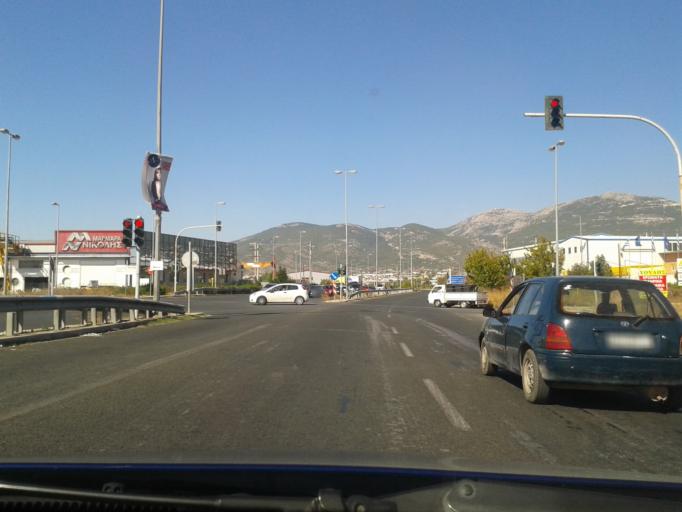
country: GR
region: Attica
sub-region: Nomarchia Athinas
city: Metamorfosi
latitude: 38.0973
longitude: 23.7705
